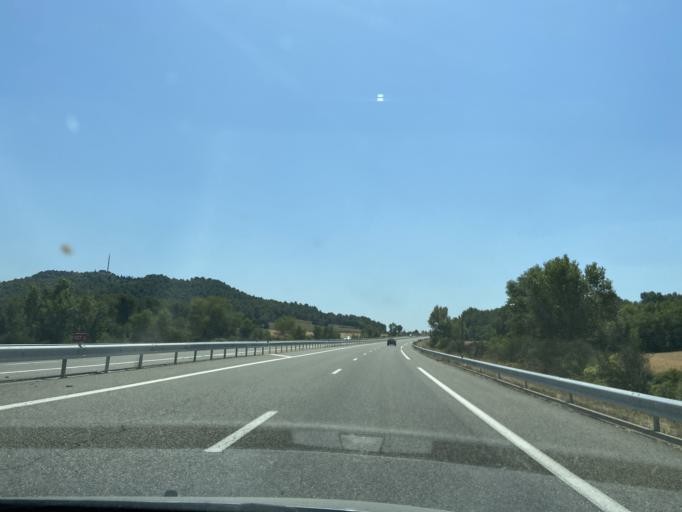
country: FR
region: Provence-Alpes-Cote d'Azur
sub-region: Departement des Alpes-de-Haute-Provence
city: Volonne
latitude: 44.1002
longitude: 5.9944
